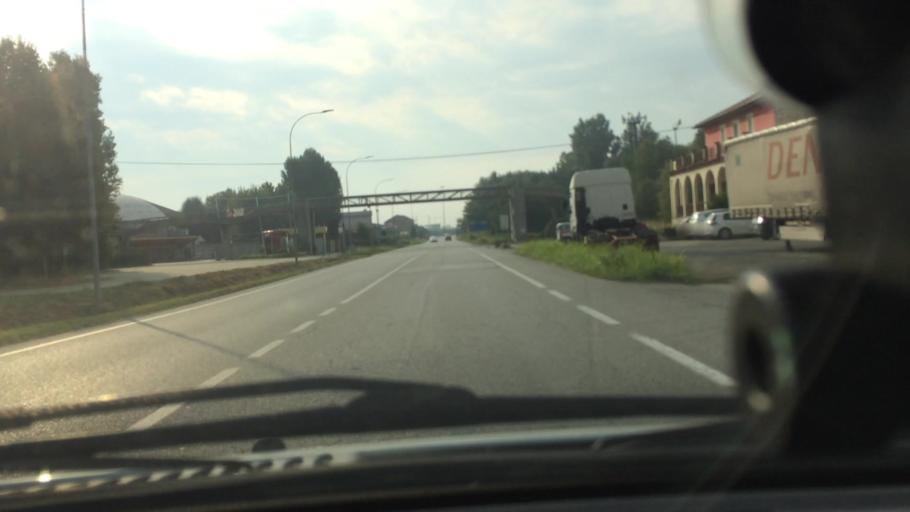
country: IT
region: Piedmont
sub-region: Provincia di Torino
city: Villastellone
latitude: 44.9195
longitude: 7.7377
